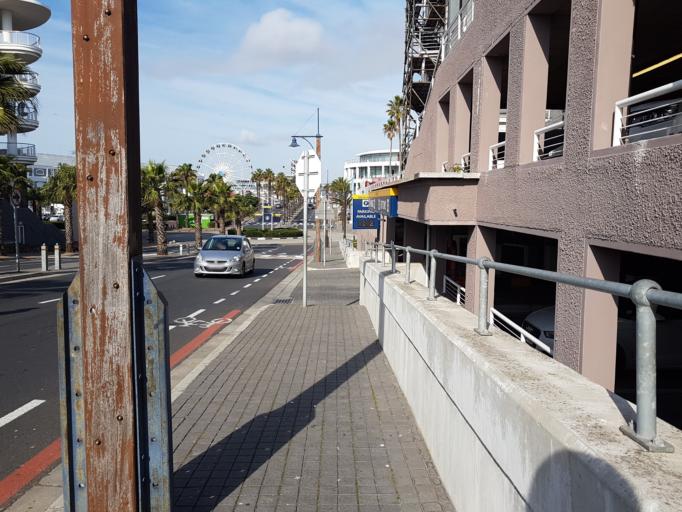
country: ZA
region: Western Cape
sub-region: City of Cape Town
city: Cape Town
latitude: -33.9035
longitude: 18.4172
